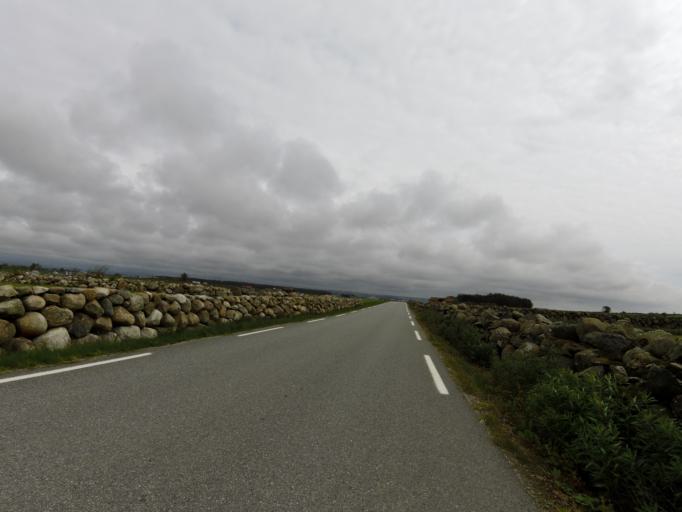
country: NO
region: Rogaland
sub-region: Ha
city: Naerbo
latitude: 58.6563
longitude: 5.5713
